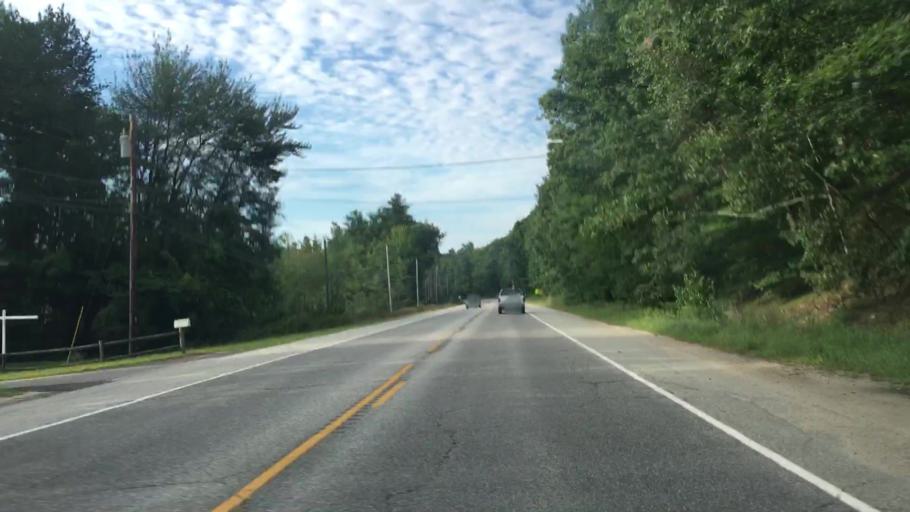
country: US
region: Maine
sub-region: Cumberland County
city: Raymond
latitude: 43.8678
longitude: -70.4655
